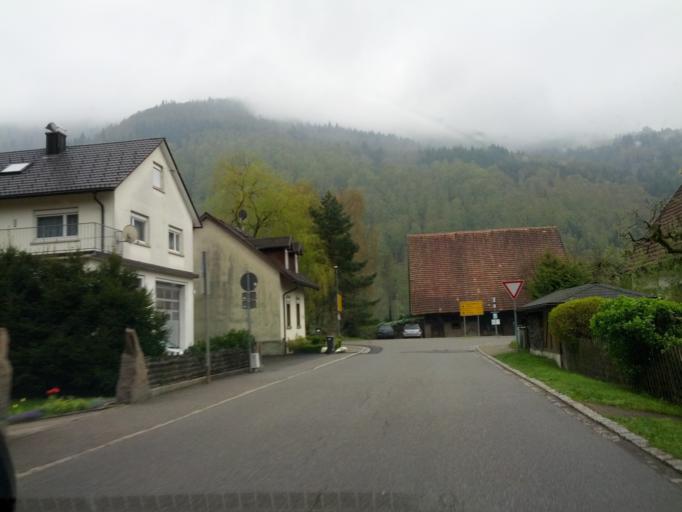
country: DE
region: Baden-Wuerttemberg
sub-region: Freiburg Region
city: Utzenfeld
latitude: 47.8020
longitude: 7.9166
